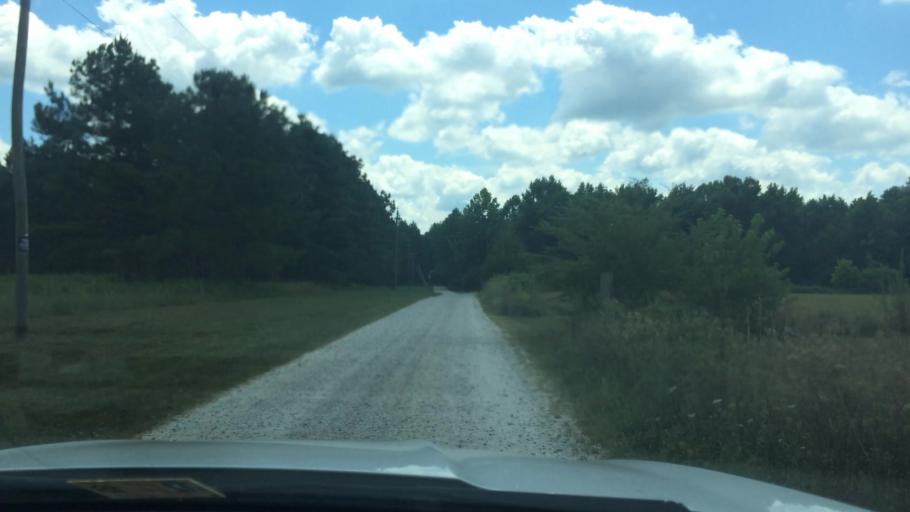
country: US
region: Virginia
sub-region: King William County
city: West Point
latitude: 37.5937
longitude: -76.7960
